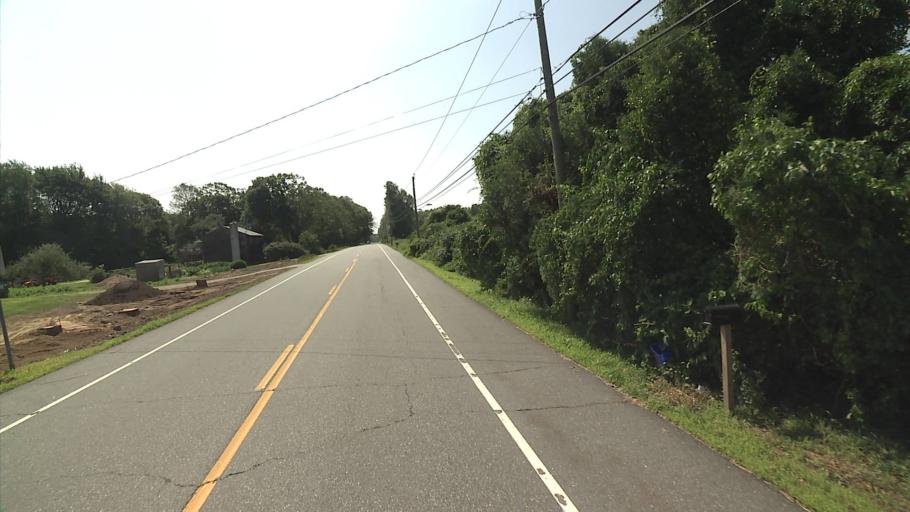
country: US
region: Connecticut
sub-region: New London County
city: Colchester
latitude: 41.5475
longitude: -72.2766
